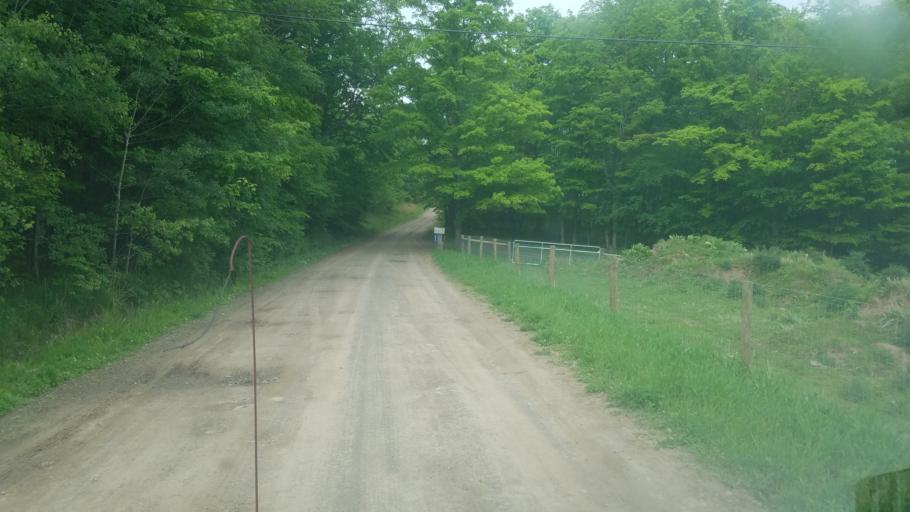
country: US
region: Pennsylvania
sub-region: Tioga County
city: Westfield
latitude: 41.9295
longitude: -77.7008
